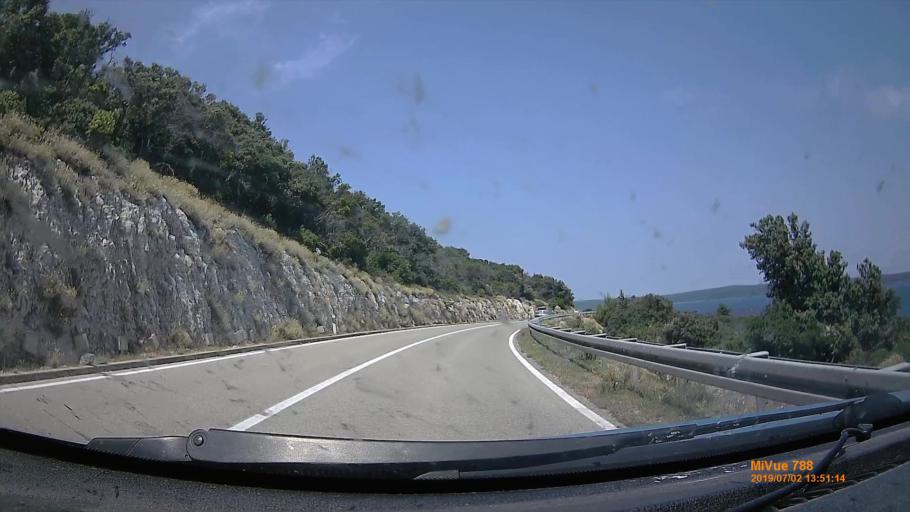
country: HR
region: Primorsko-Goranska
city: Mali Losinj
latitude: 44.6031
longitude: 14.4041
